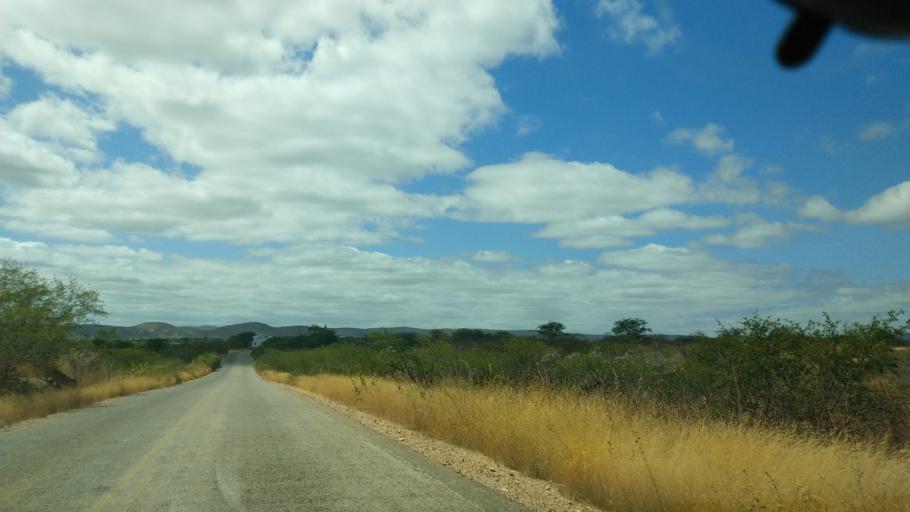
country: BR
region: Rio Grande do Norte
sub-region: Currais Novos
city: Currais Novos
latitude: -6.2709
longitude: -36.5524
